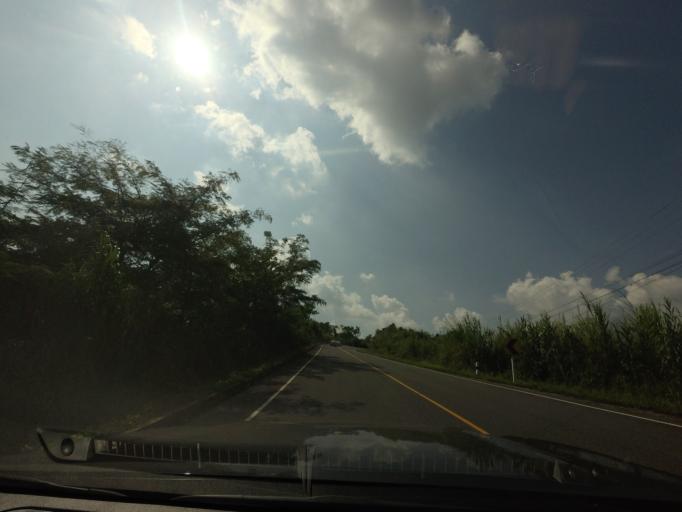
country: TH
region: Nan
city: Santi Suk
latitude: 18.9779
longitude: 101.0065
